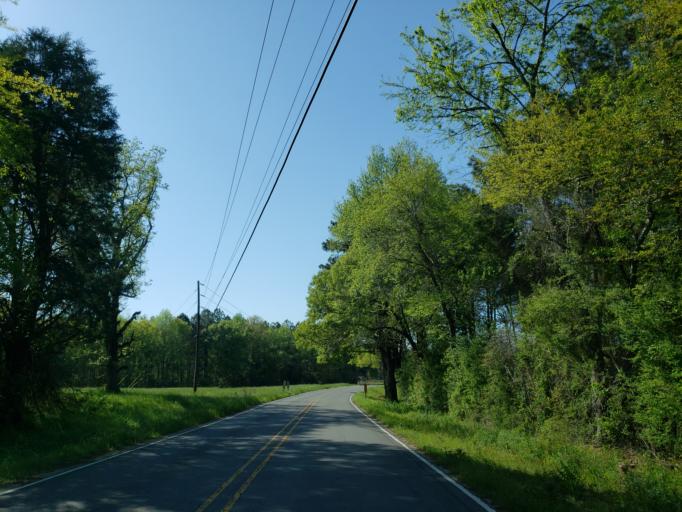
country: US
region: Mississippi
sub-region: Forrest County
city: Rawls Springs
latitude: 31.4928
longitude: -89.3541
